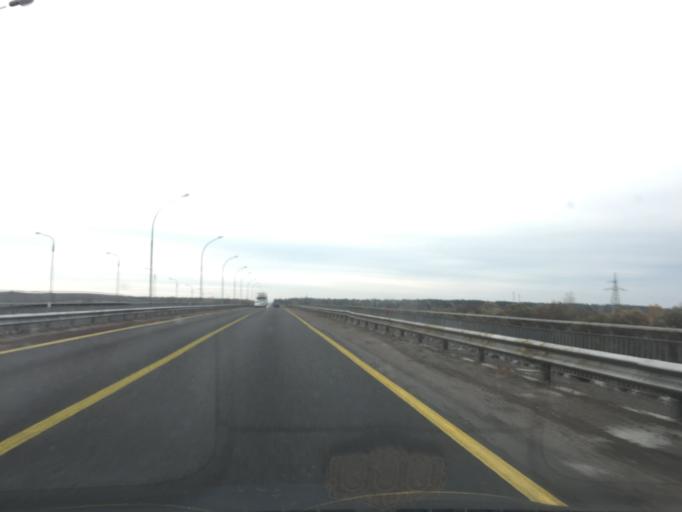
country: BY
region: Gomel
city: Horad Rechytsa
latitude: 52.3221
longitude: 30.5251
